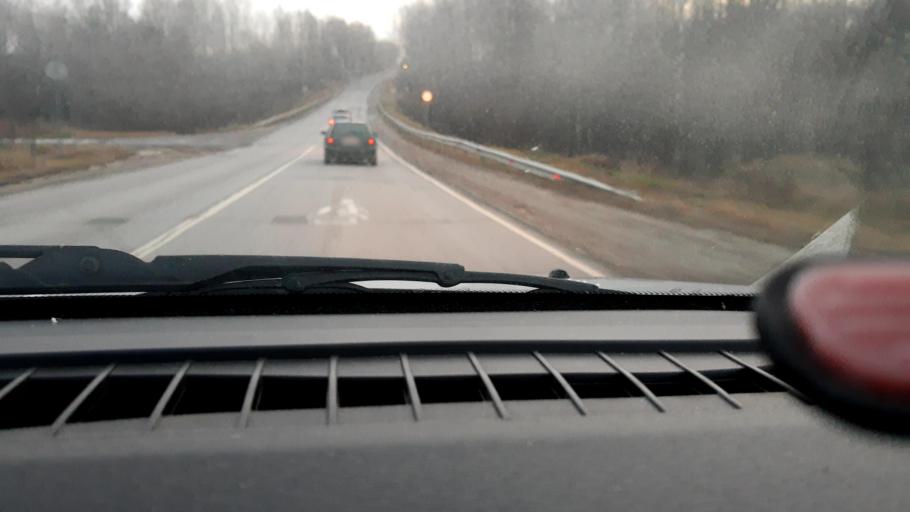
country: RU
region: Nizjnij Novgorod
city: Krasnyye Baki
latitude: 57.0640
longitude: 45.1375
